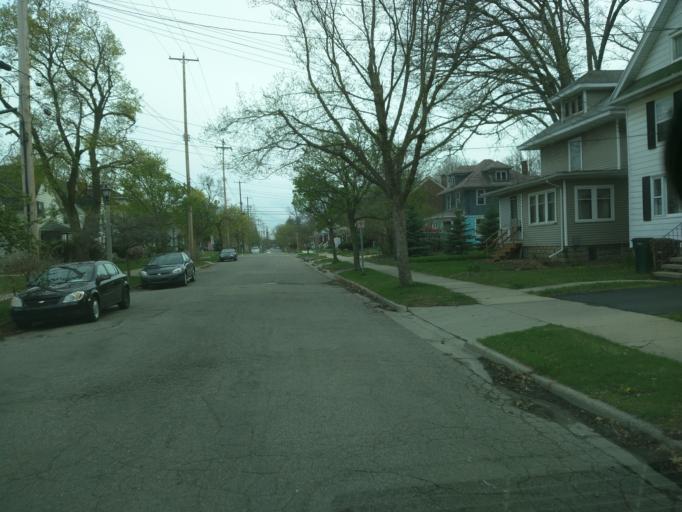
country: US
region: Michigan
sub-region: Ingham County
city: Lansing
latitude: 42.7319
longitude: -84.5330
